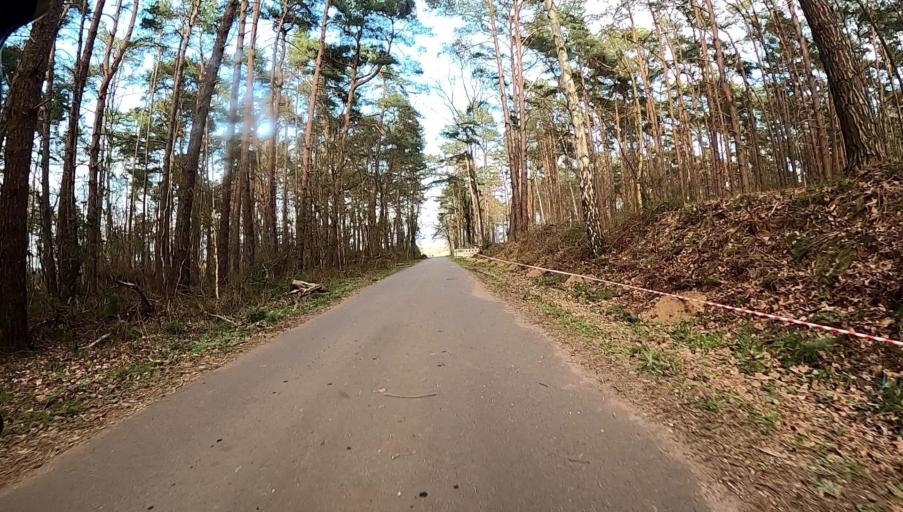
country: DE
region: Lower Saxony
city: Lindwedel
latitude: 52.5429
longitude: 9.6206
